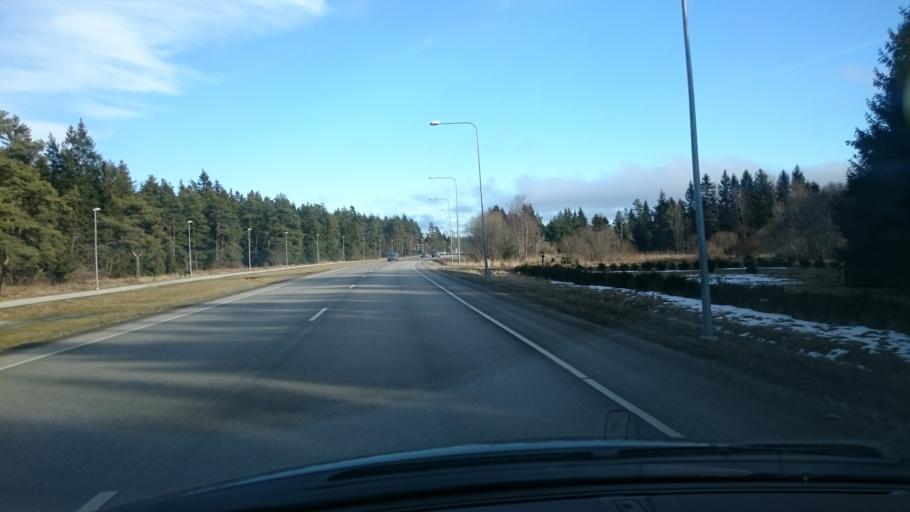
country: EE
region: Harju
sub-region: Harku vald
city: Tabasalu
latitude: 59.4379
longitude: 24.5062
